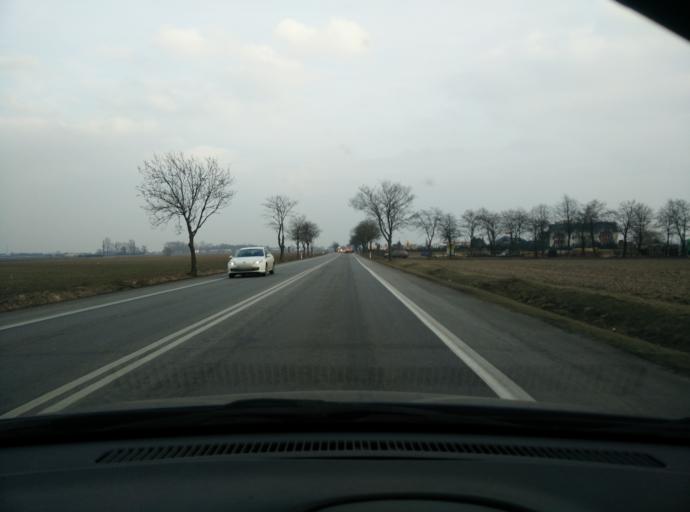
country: PL
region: Greater Poland Voivodeship
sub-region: Powiat sredzki
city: Zaniemysl
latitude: 52.2350
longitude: 17.1729
